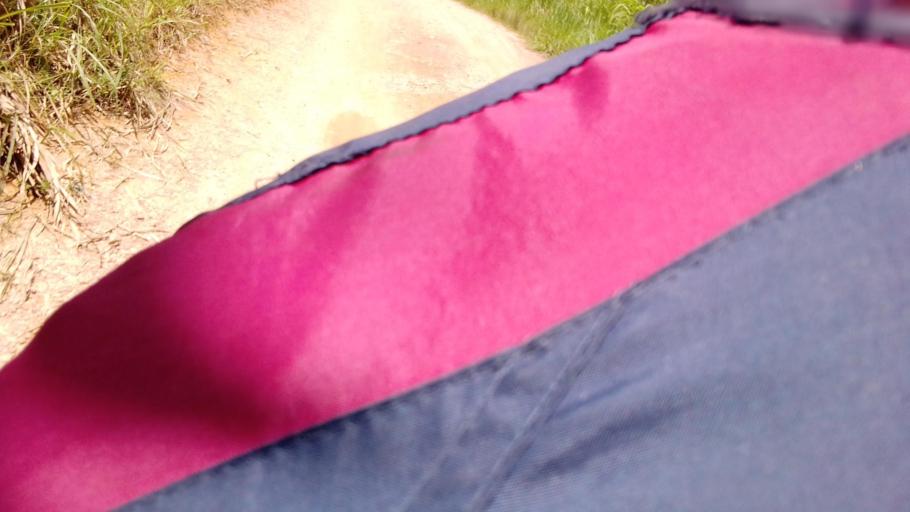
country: SL
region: Eastern Province
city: Koidu
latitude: 8.6886
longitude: -10.9556
